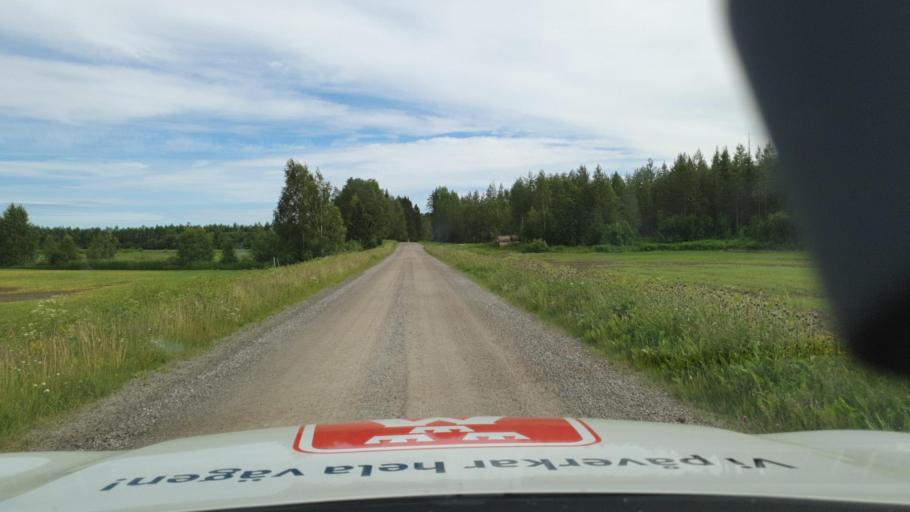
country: SE
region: Vaesterbotten
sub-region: Robertsfors Kommun
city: Robertsfors
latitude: 64.3887
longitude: 21.0337
